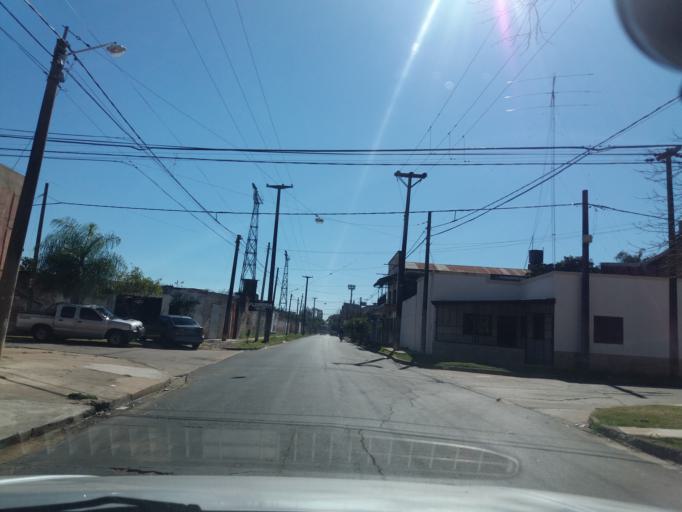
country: AR
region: Corrientes
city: Corrientes
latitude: -27.4835
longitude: -58.8442
